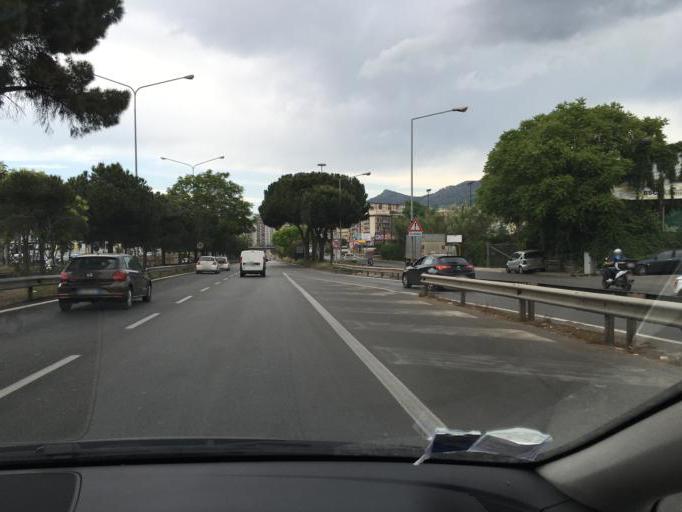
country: IT
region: Sicily
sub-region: Palermo
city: Palermo
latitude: 38.1365
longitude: 13.3309
